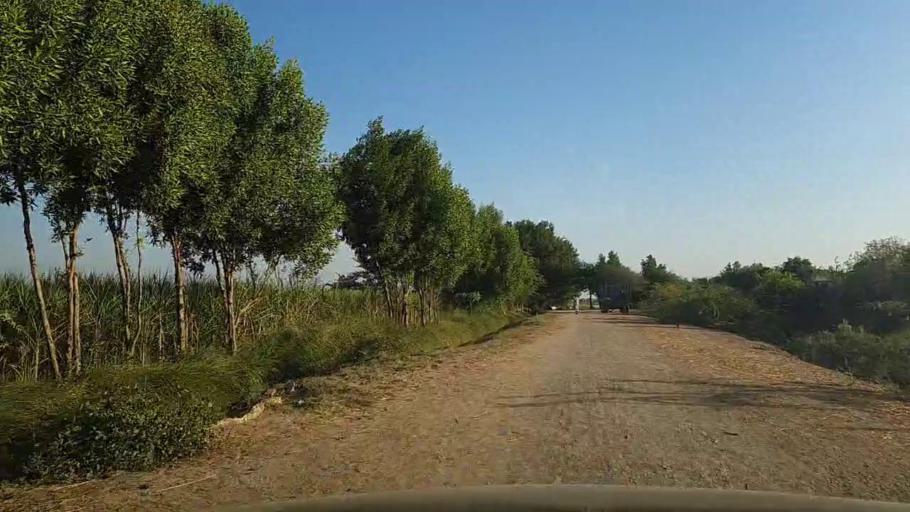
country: PK
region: Sindh
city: Mirpur Batoro
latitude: 24.7085
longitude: 68.3209
